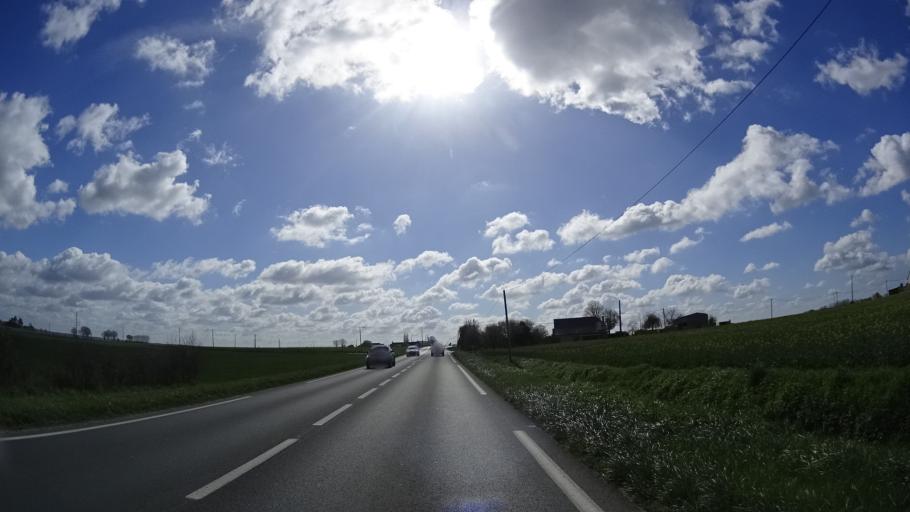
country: FR
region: Pays de la Loire
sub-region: Departement de Maine-et-Loire
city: Brissac-Quince
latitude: 47.3285
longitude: -0.4196
